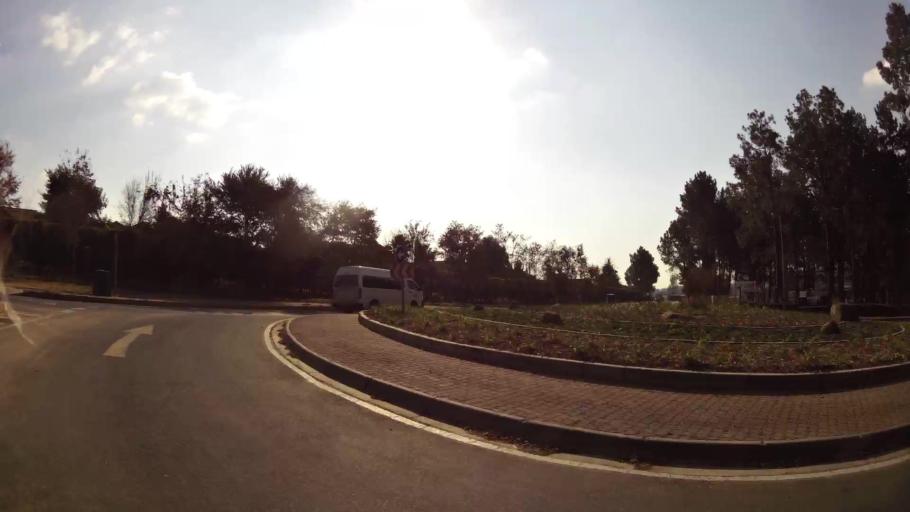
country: ZA
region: Gauteng
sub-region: City of Johannesburg Metropolitan Municipality
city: Modderfontein
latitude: -26.1031
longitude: 28.1517
